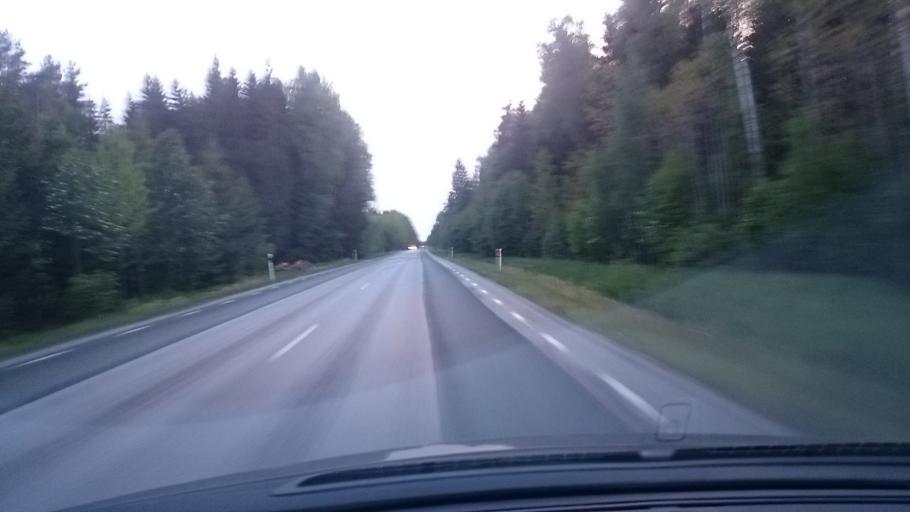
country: EE
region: Paernumaa
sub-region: Vaendra vald (alev)
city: Vandra
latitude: 58.8305
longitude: 25.1037
